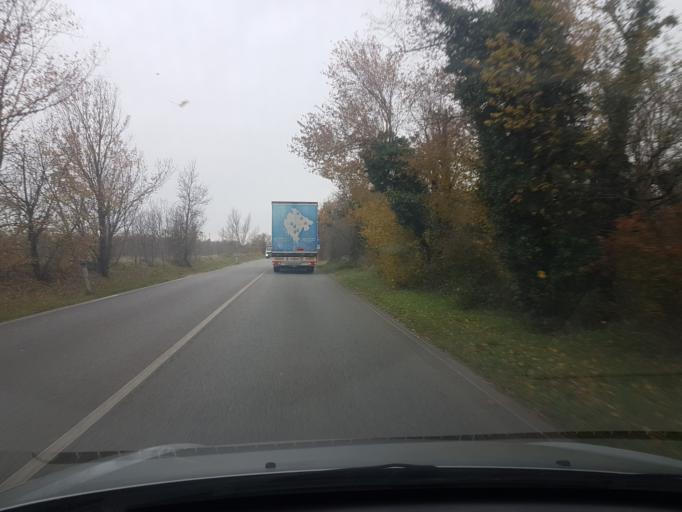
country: IT
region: Friuli Venezia Giulia
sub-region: Provincia di Trieste
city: Prosecco-Contovello
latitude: 45.7100
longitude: 13.7418
